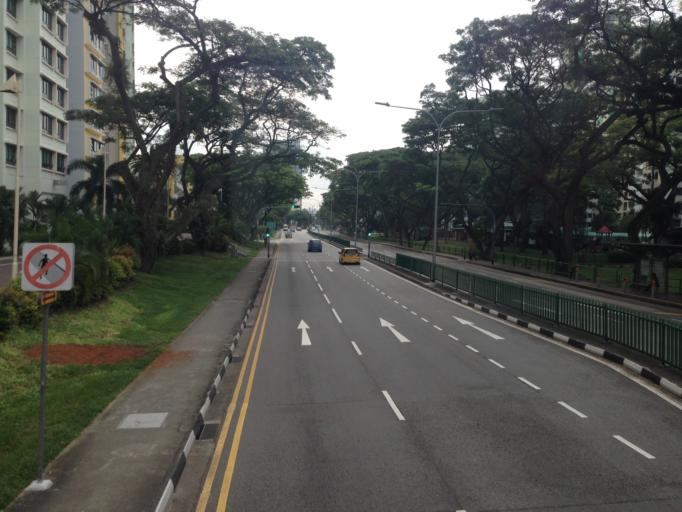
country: SG
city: Singapore
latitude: 1.2904
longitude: 103.8291
